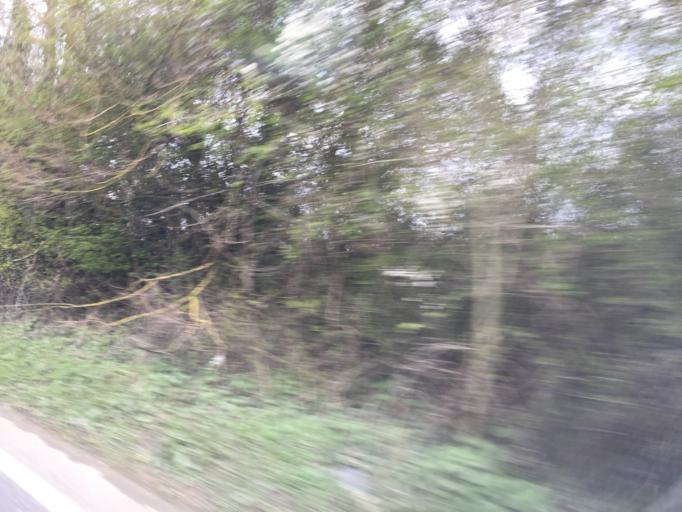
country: GB
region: England
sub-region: Northamptonshire
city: Brackley
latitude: 51.9678
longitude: -1.0928
